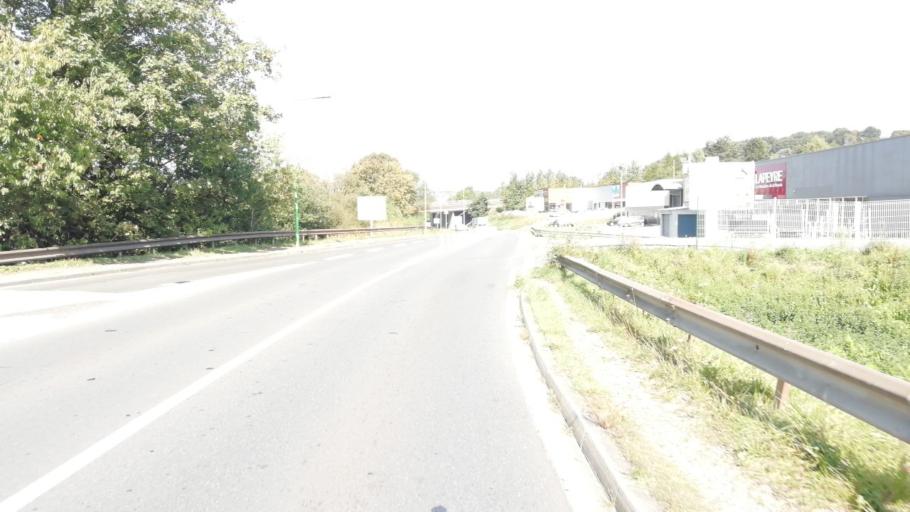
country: FR
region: Haute-Normandie
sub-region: Departement de la Seine-Maritime
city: Montivilliers
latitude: 49.5310
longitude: 0.1886
